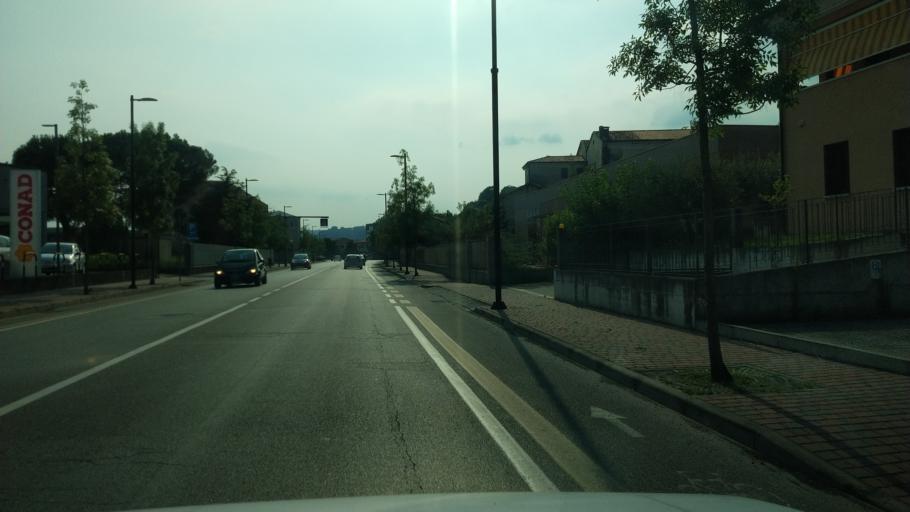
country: IT
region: Veneto
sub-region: Provincia di Vicenza
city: Bassano del Grappa
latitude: 45.7650
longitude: 11.7208
